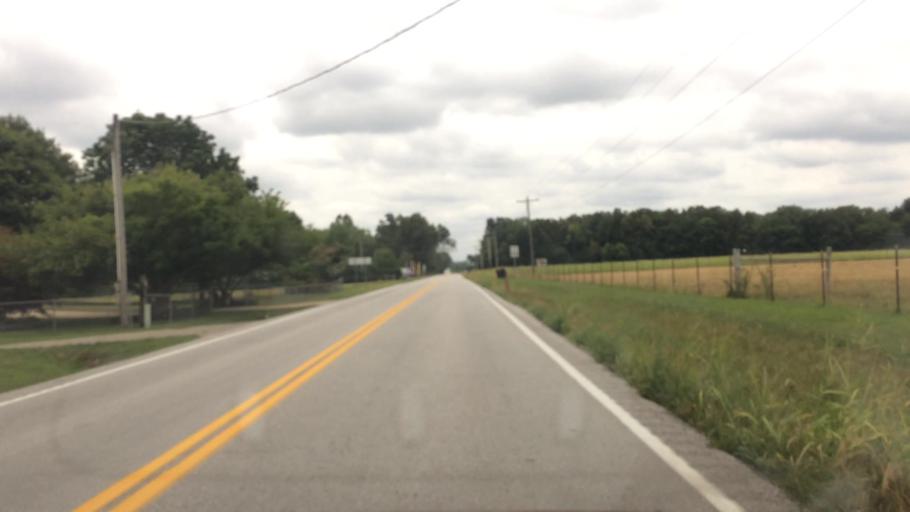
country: US
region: Missouri
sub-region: Greene County
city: Strafford
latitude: 37.2951
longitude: -93.1130
